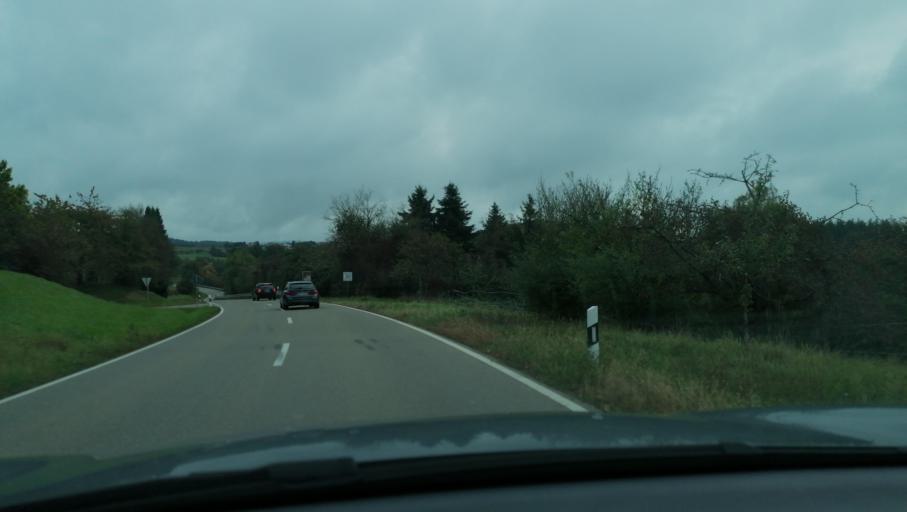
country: DE
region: Baden-Wuerttemberg
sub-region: Regierungsbezirk Stuttgart
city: Winterbach
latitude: 48.8479
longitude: 9.4871
